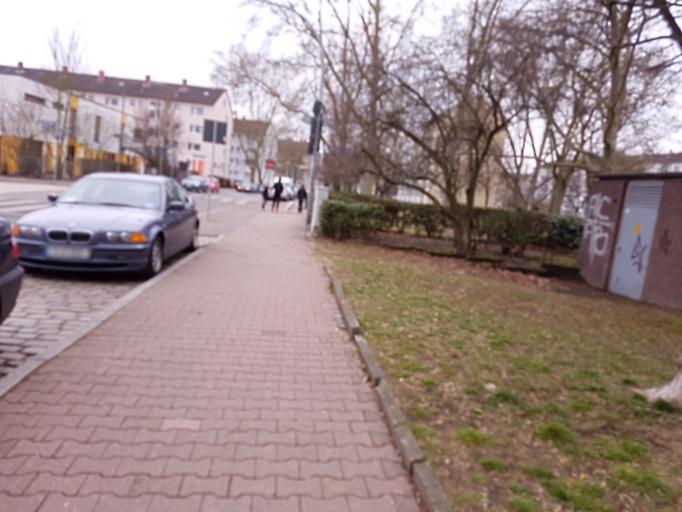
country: DE
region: Hesse
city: Niederrad
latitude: 50.0805
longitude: 8.6427
